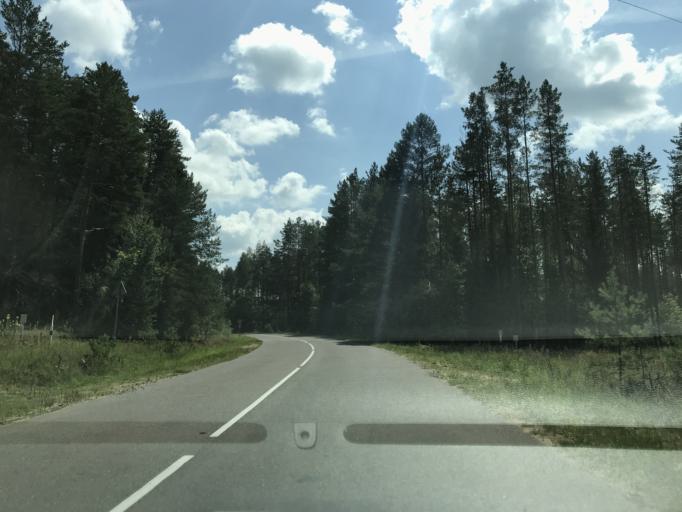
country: BY
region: Minsk
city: Rakaw
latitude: 53.9974
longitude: 26.9867
